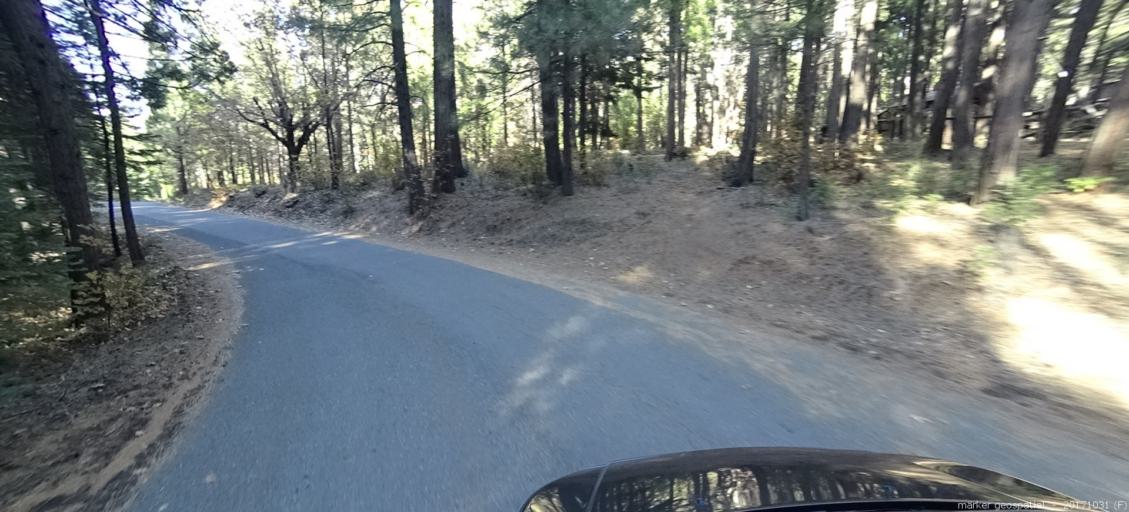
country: US
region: California
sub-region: Shasta County
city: Shingletown
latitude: 40.4923
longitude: -121.9106
